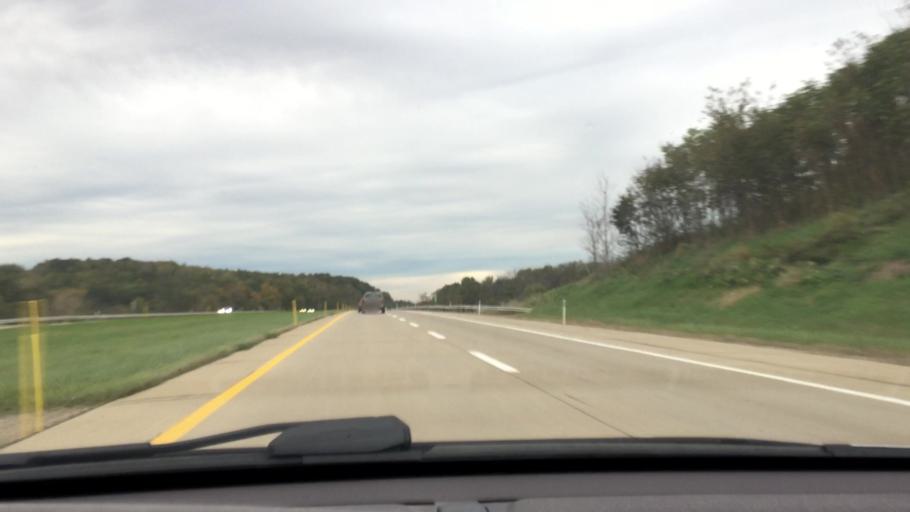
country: US
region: Pennsylvania
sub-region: Lawrence County
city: New Beaver
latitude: 40.8571
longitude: -80.3687
